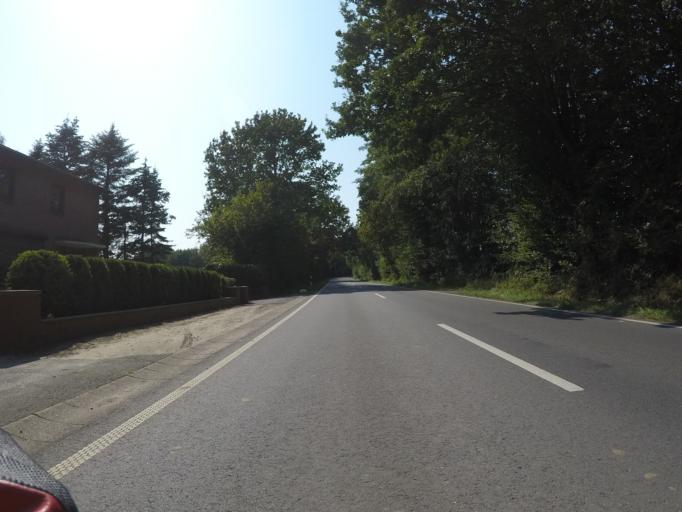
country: DE
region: Schleswig-Holstein
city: Huttblek
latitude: 53.8441
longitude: 10.0695
